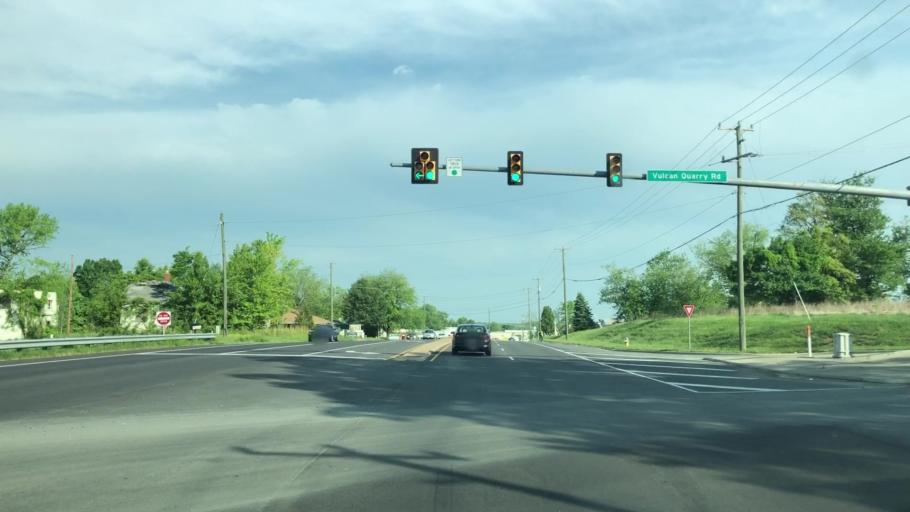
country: US
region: Virginia
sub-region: Stafford County
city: Stafford
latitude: 38.4723
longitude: -77.4666
